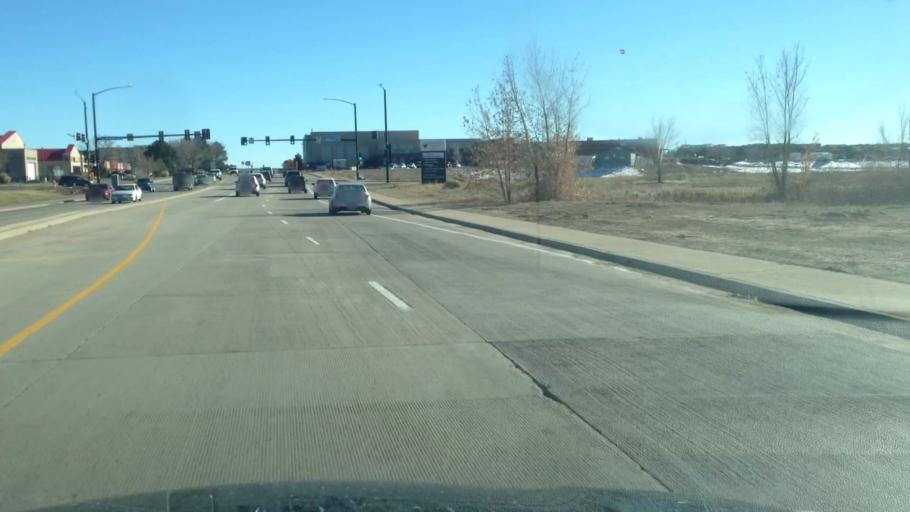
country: US
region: Colorado
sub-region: Arapahoe County
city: Dove Valley
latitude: 39.5933
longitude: -104.8202
